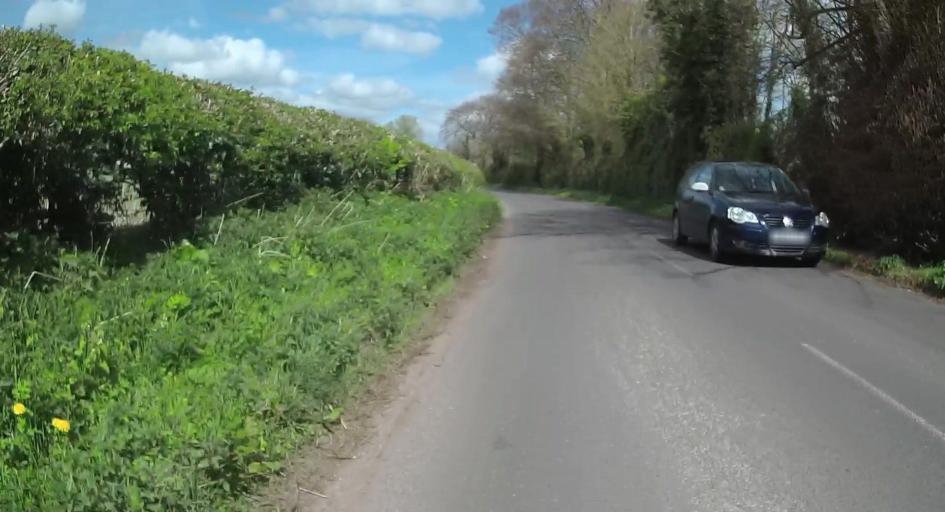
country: GB
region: England
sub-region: Hampshire
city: Abbotts Ann
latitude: 51.1095
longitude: -1.5002
